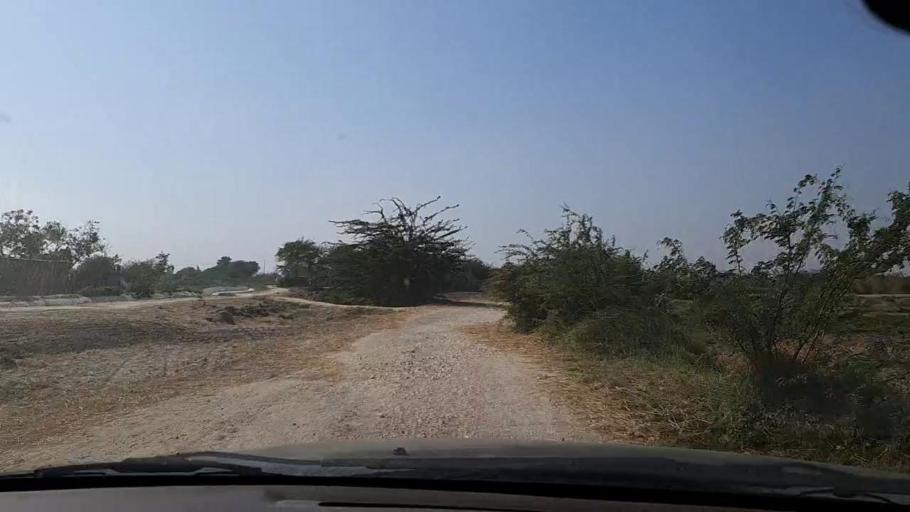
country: PK
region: Sindh
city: Chuhar Jamali
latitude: 24.4278
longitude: 67.8011
